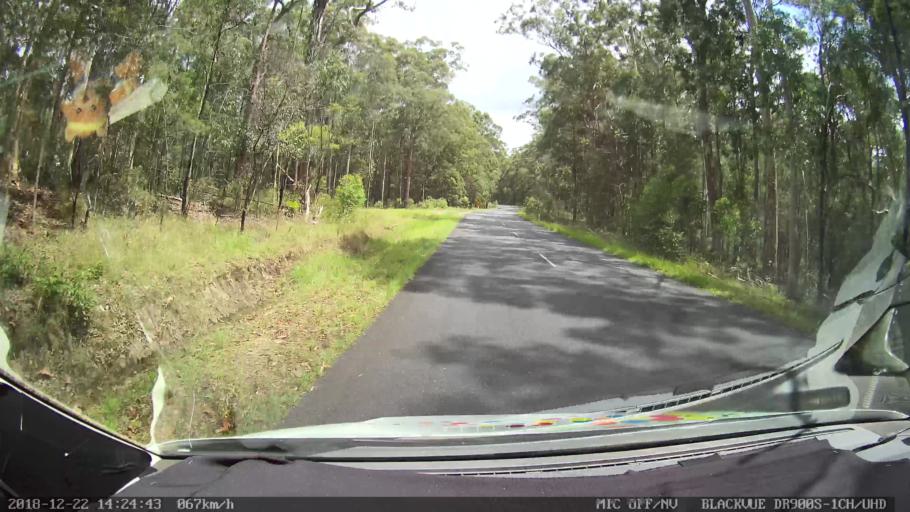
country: AU
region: New South Wales
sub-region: Bellingen
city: Dorrigo
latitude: -30.0460
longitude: 152.6426
